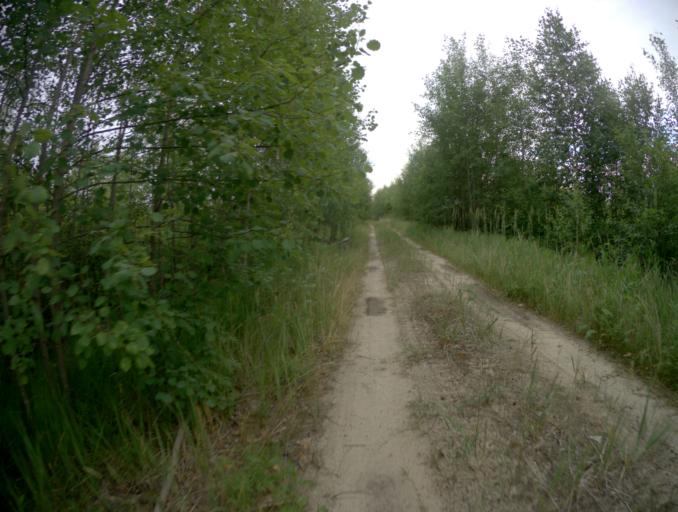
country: RU
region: Nizjnij Novgorod
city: Frolishchi
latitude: 56.5382
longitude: 42.6426
